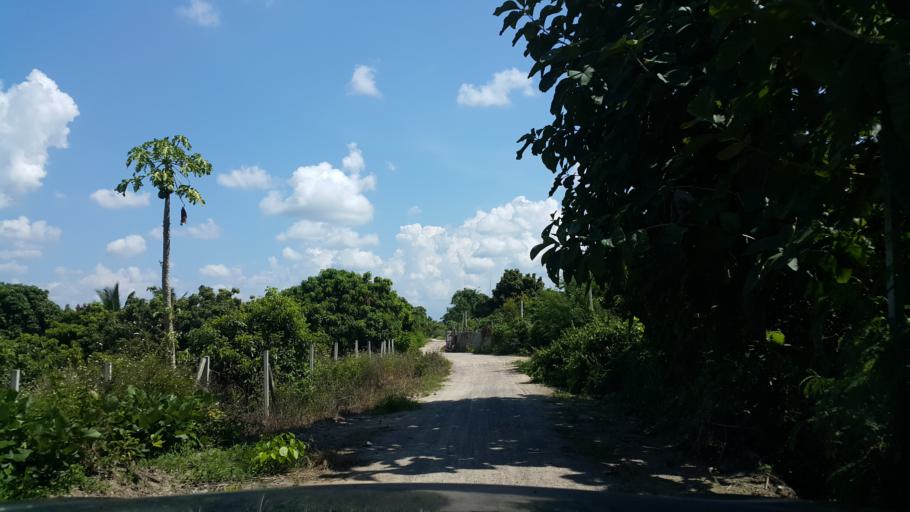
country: TH
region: Chiang Mai
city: Chom Thong
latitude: 18.4172
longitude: 98.6849
